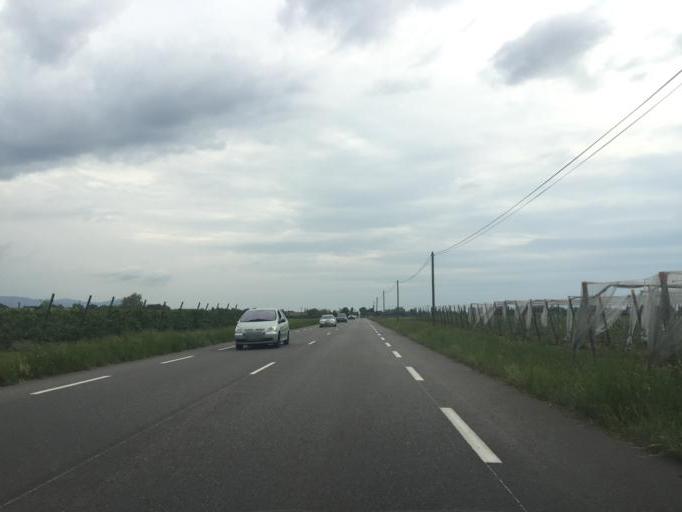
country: FR
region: Rhone-Alpes
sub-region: Departement de la Drome
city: Alixan
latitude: 44.9929
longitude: 5.0329
